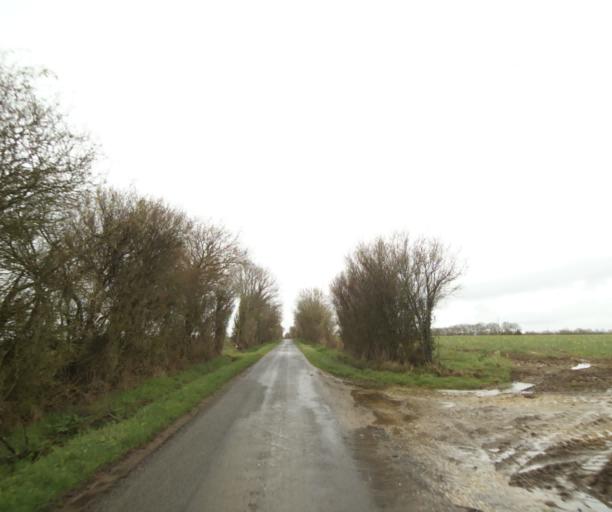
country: FR
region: Pays de la Loire
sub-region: Departement de la Loire-Atlantique
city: Bouvron
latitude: 47.4484
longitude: -1.8783
